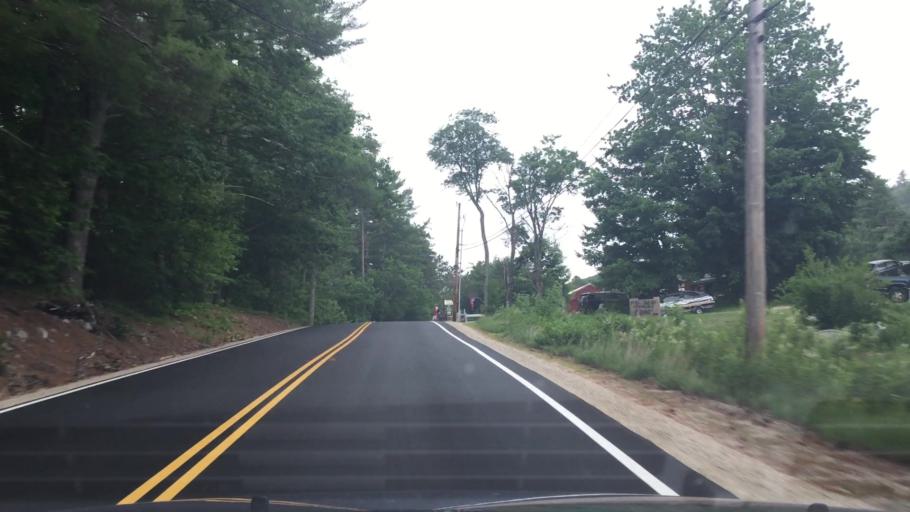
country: US
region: New Hampshire
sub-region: Carroll County
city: Madison
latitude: 43.8763
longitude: -71.0841
